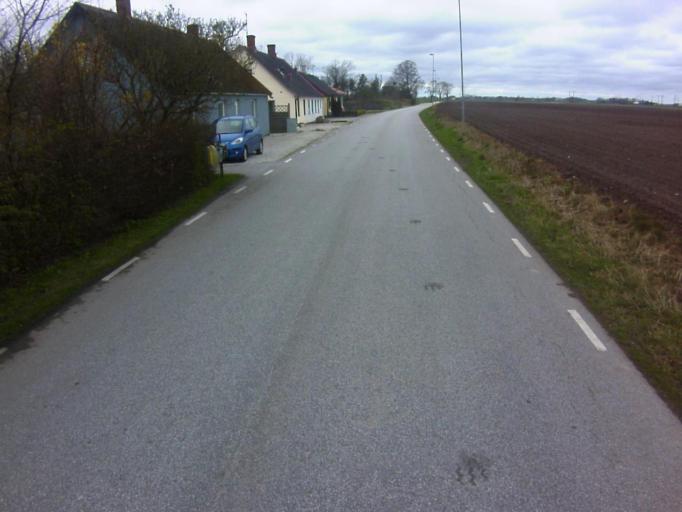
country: SE
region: Skane
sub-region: Kavlinge Kommun
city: Kaevlinge
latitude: 55.7941
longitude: 13.1970
